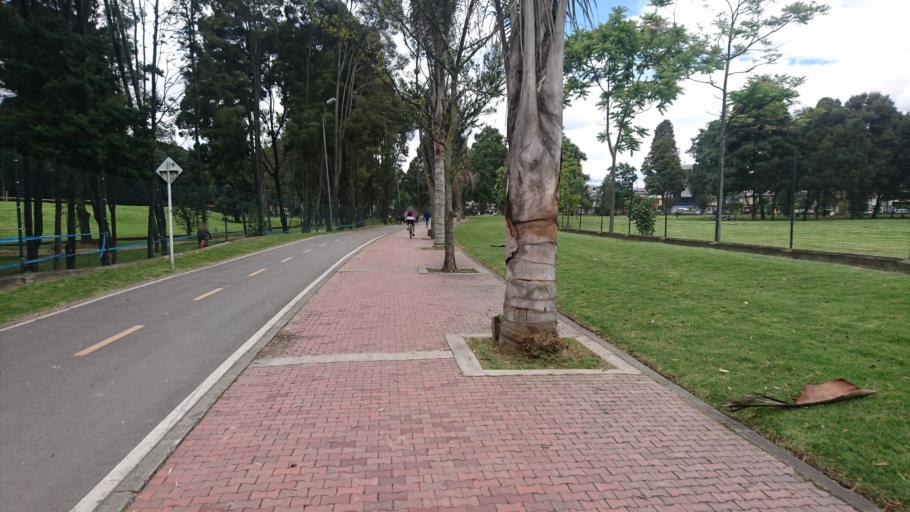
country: CO
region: Bogota D.C.
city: Bogota
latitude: 4.6581
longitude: -74.0989
